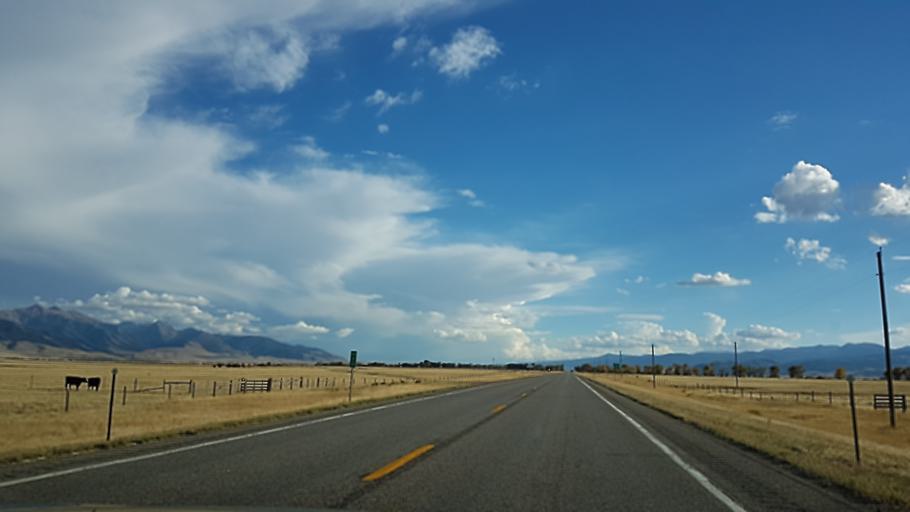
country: US
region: Montana
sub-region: Madison County
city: Virginia City
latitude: 45.2187
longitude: -111.6789
